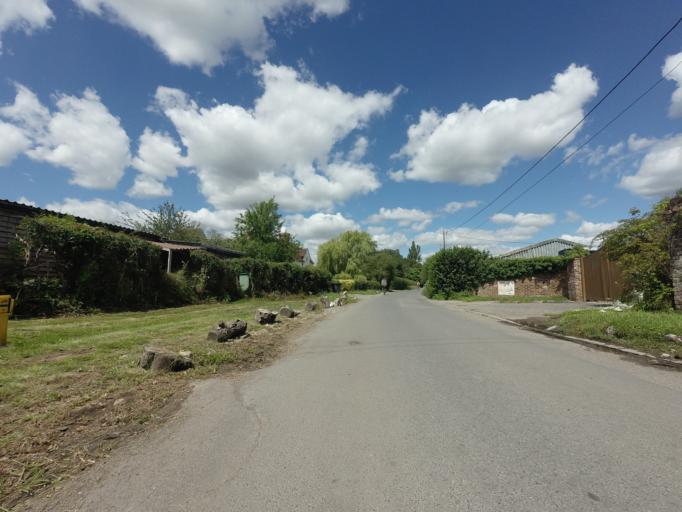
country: GB
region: England
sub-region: East Sussex
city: Hailsham
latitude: 50.8656
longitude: 0.1575
